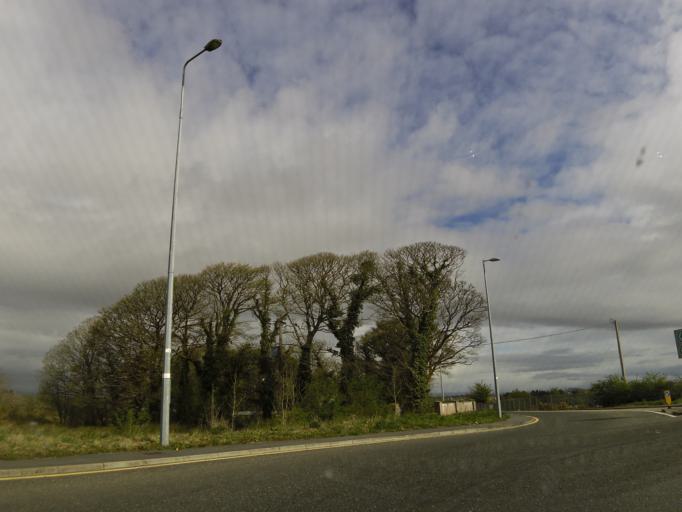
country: IE
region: Connaught
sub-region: Sligo
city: Tobercurry
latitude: 53.9555
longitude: -8.7936
